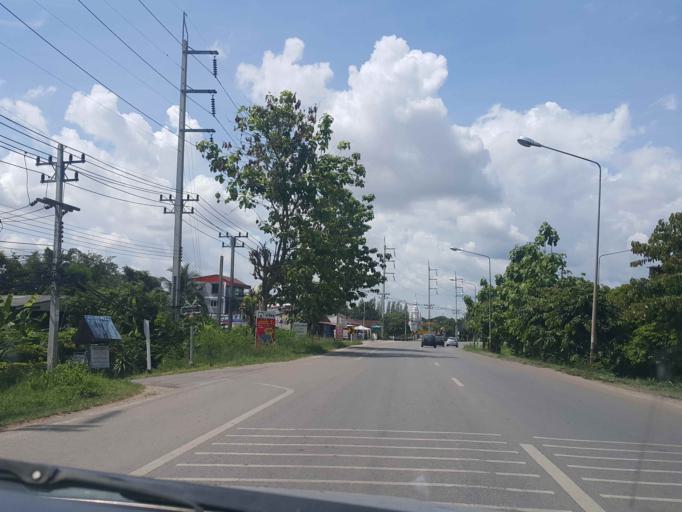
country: TH
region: Phayao
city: Phayao
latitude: 19.1592
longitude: 99.9144
